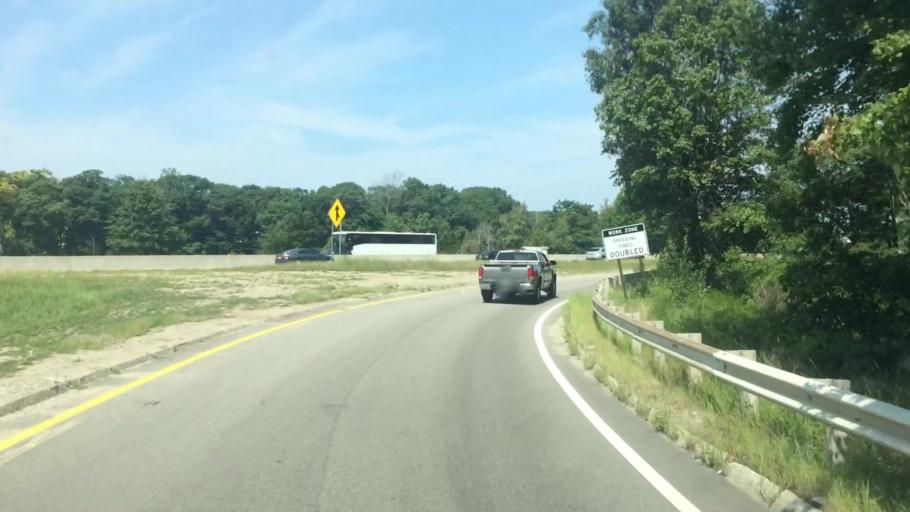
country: US
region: Massachusetts
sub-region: Norfolk County
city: Needham
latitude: 42.2713
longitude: -71.1986
